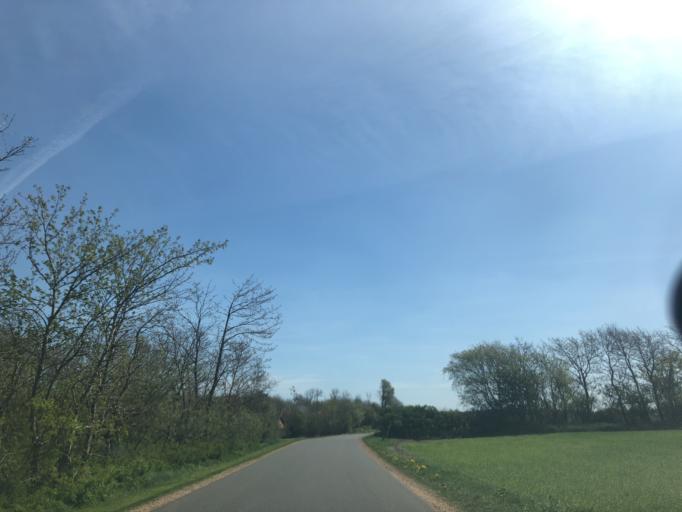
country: DK
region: Central Jutland
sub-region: Holstebro Kommune
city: Vinderup
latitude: 56.5341
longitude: 8.8182
